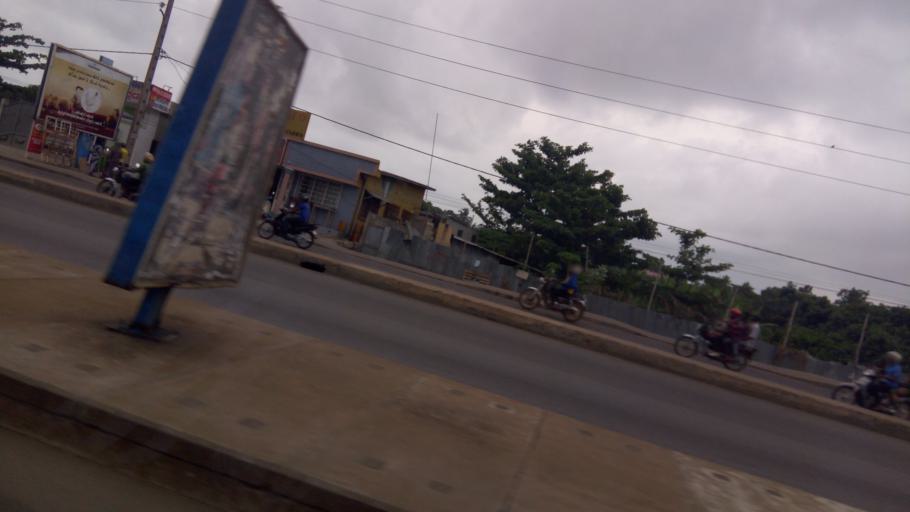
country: BJ
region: Littoral
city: Cotonou
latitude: 6.3877
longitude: 2.3676
